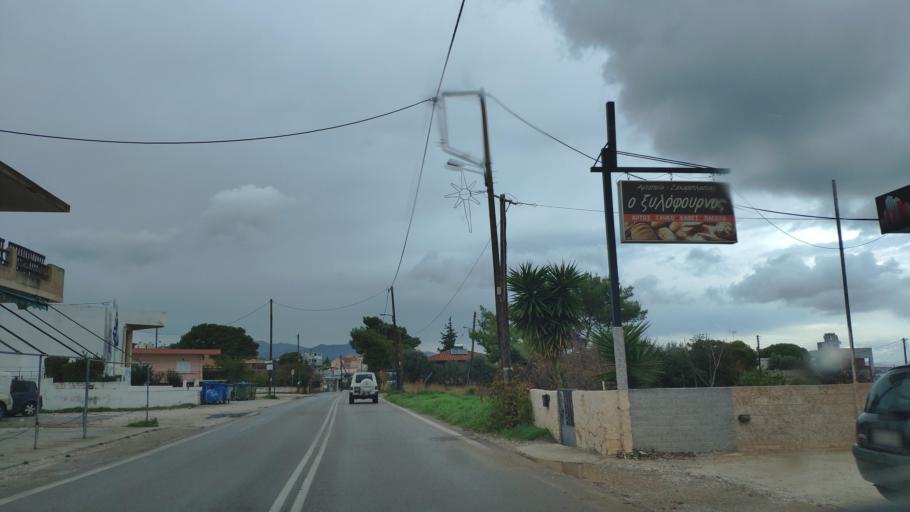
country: GR
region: Attica
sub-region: Nomarchia Anatolikis Attikis
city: Artemida
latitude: 37.9520
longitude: 24.0073
